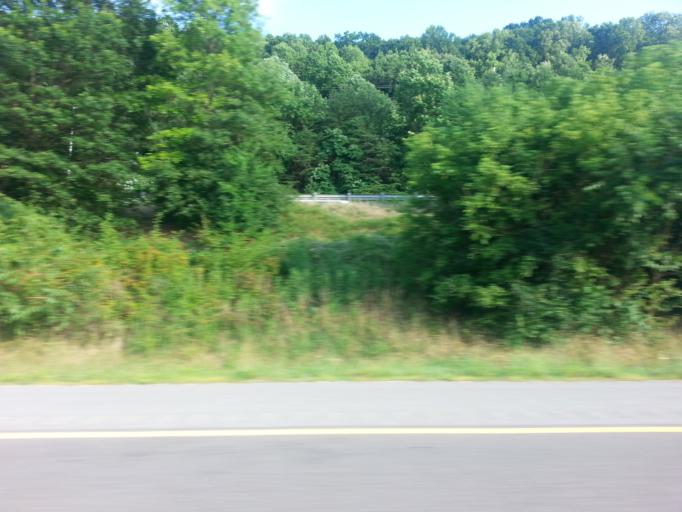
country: US
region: Tennessee
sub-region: Knox County
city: Knoxville
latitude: 36.0272
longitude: -83.9024
